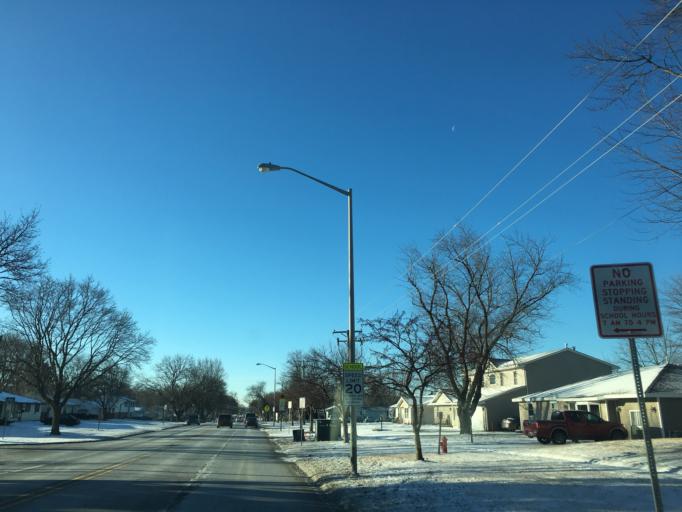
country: US
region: Illinois
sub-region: DuPage County
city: Hanover Park
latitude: 42.0211
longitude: -88.1192
